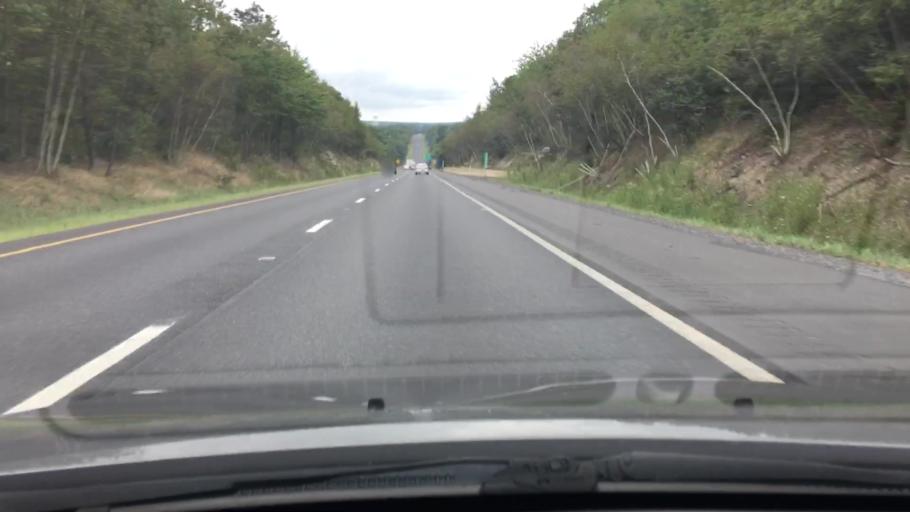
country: US
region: Pennsylvania
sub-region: Schuylkill County
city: Mahanoy City
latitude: 40.7811
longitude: -76.1756
